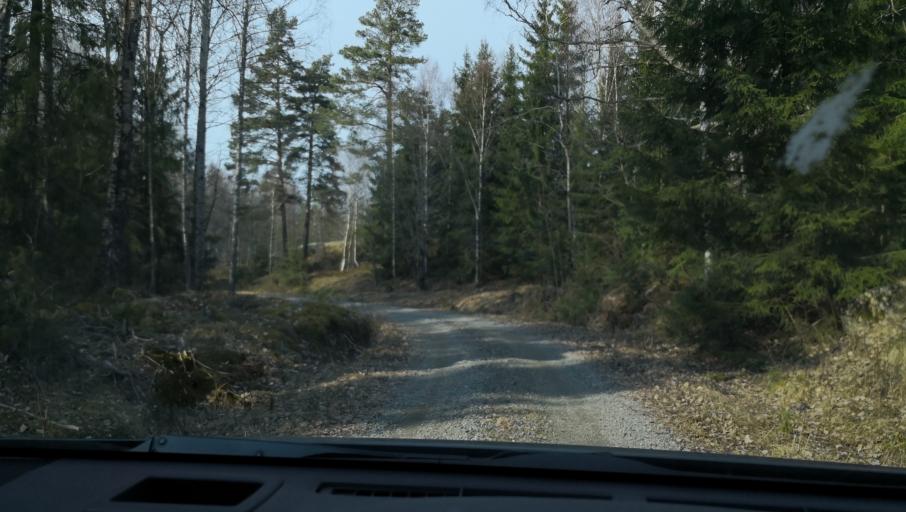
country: SE
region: OErebro
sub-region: Lindesbergs Kommun
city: Frovi
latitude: 59.3864
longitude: 15.4039
